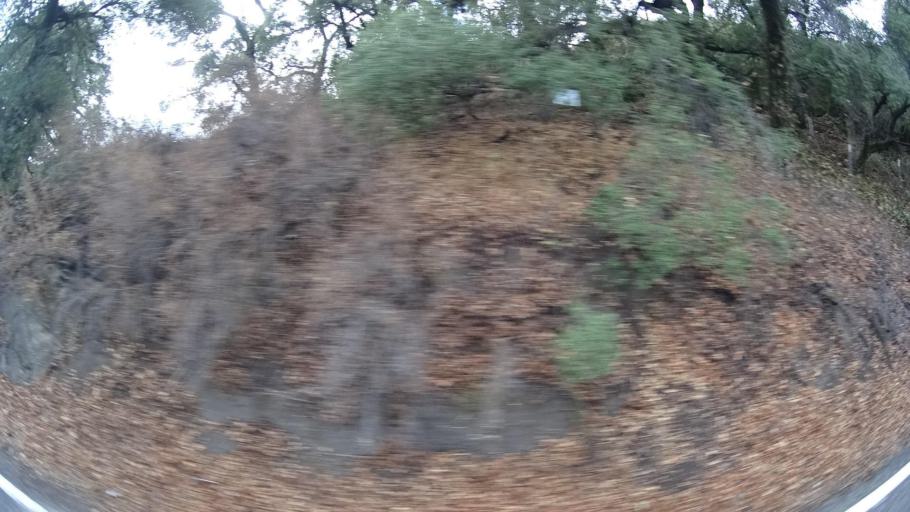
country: MX
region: Baja California
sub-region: Tecate
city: Hacienda Tecate
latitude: 32.5904
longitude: -116.5139
